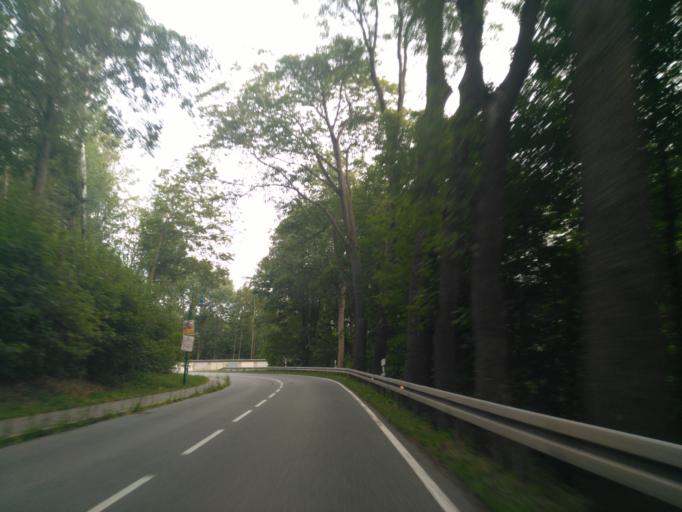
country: DE
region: Saxony
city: Tannenberg
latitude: 50.6041
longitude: 12.9493
